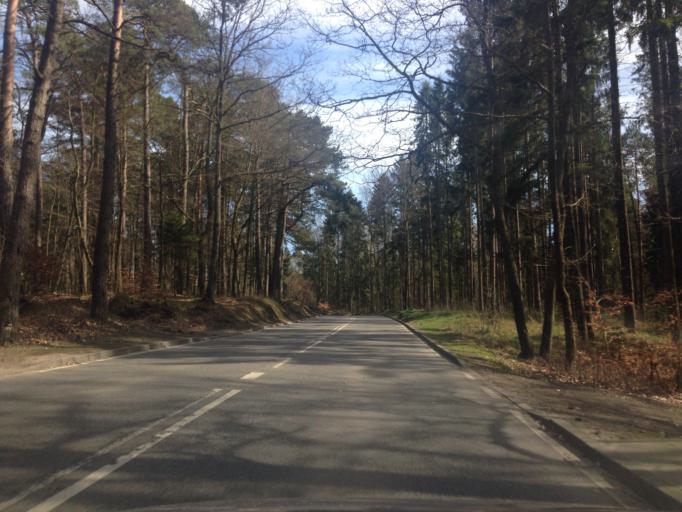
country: PL
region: Pomeranian Voivodeship
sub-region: Gdynia
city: Wielki Kack
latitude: 54.4782
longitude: 18.4512
